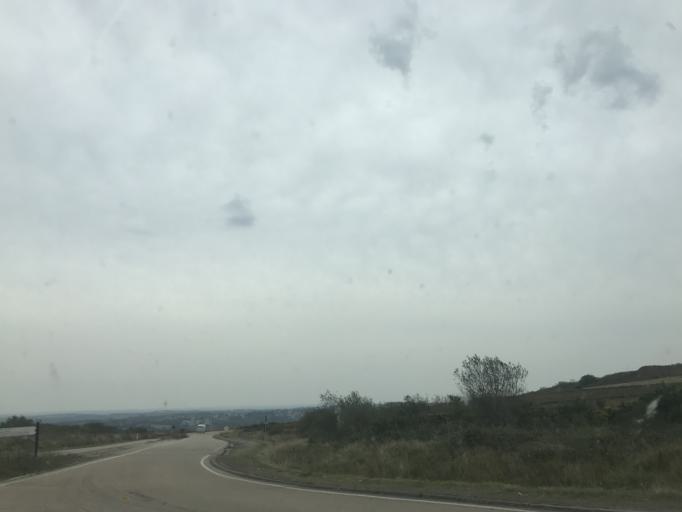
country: FR
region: Brittany
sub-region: Departement du Finistere
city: Plouneour-Menez
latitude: 48.4119
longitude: -3.8954
